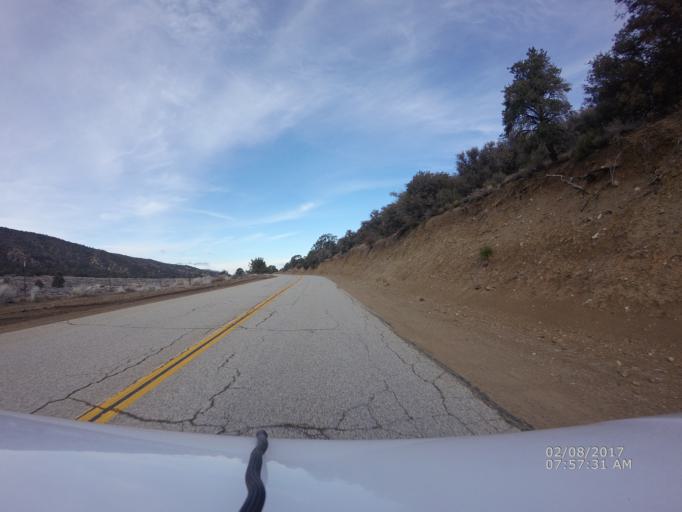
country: US
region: California
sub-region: San Bernardino County
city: Pinon Hills
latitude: 34.4157
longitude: -117.7800
